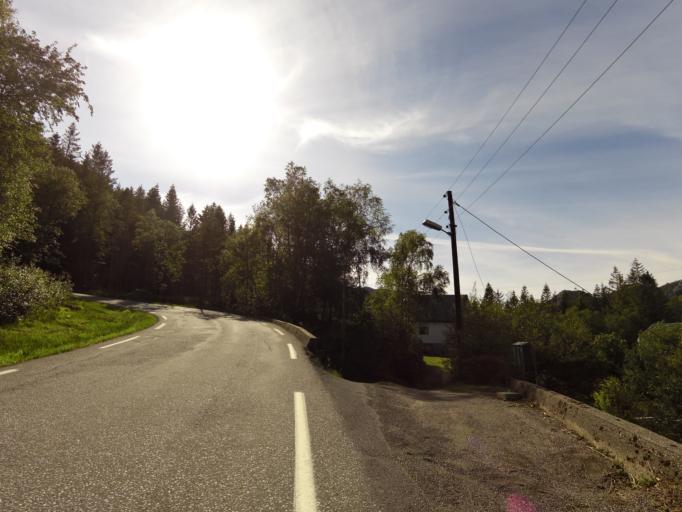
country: NO
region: Rogaland
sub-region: Sokndal
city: Hauge i Dalane
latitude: 58.3150
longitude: 6.3437
